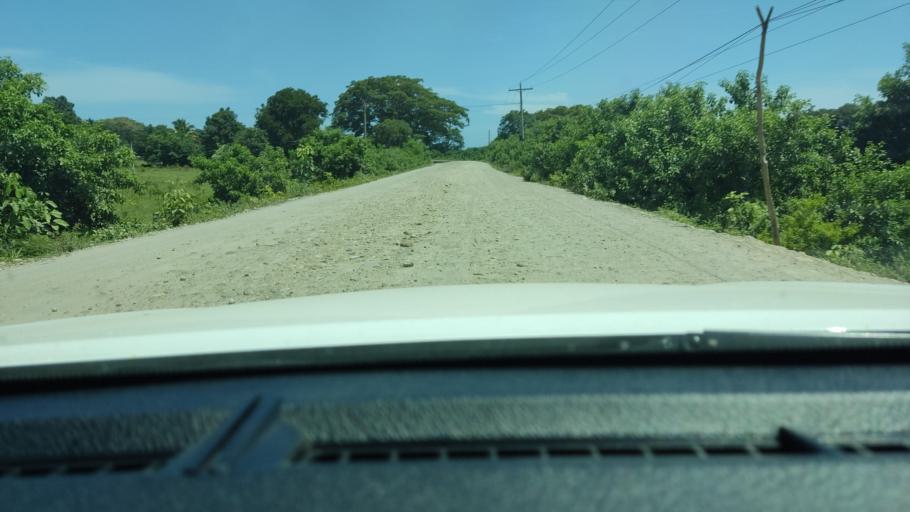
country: SV
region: Ahuachapan
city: San Francisco Menendez
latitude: 13.7877
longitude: -90.1186
